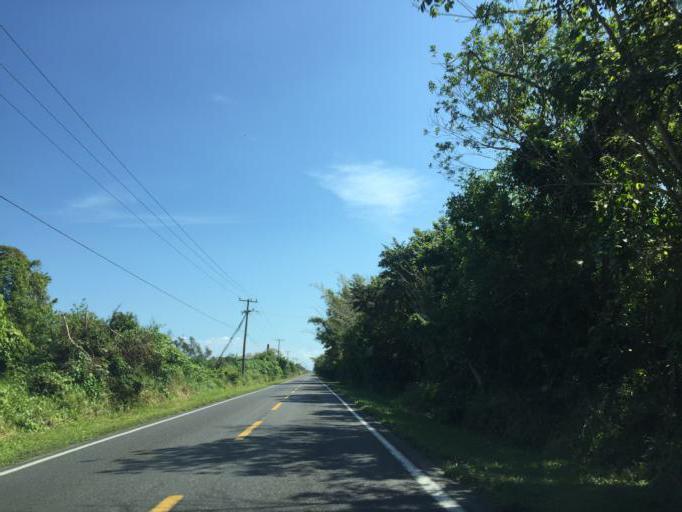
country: MX
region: Veracruz
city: Tecolutla
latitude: 20.4758
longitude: -97.0377
